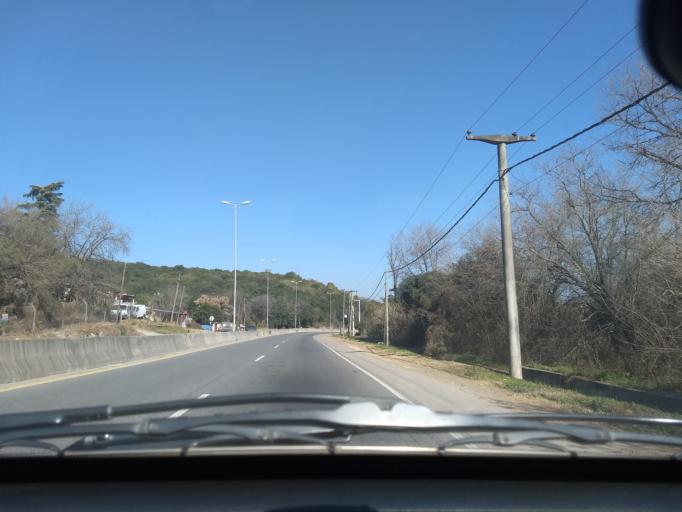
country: AR
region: Cordoba
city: Rio Ceballos
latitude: -31.1667
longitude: -64.3020
